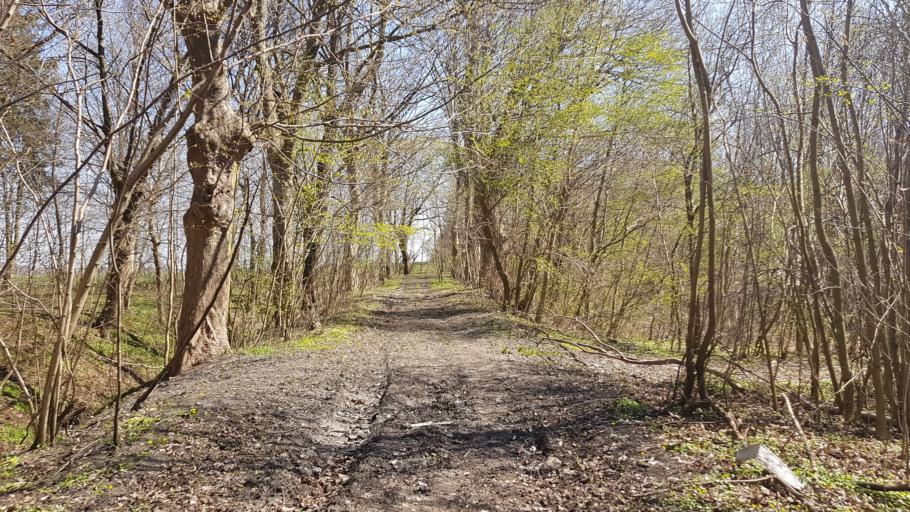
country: PL
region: Pomeranian Voivodeship
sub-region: Powiat slupski
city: Ustka
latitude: 54.5156
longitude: 16.7342
